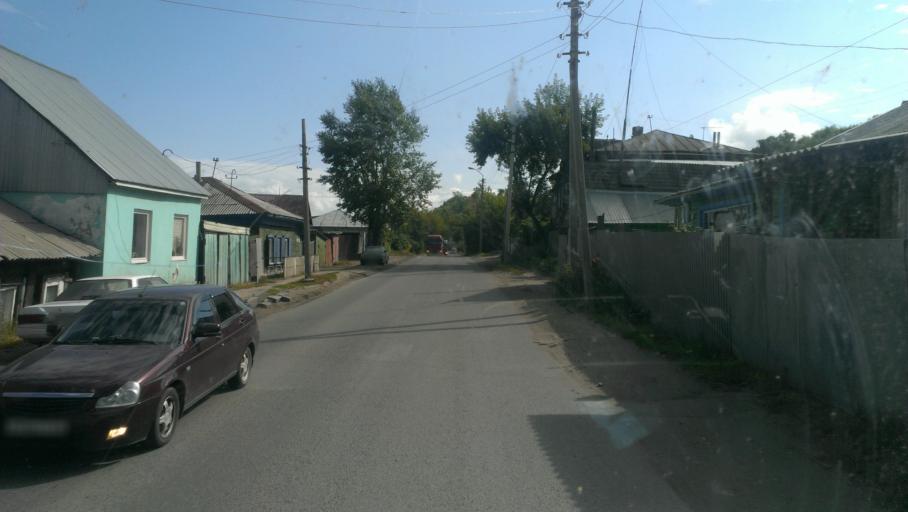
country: RU
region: Altai Krai
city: Zaton
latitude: 53.3197
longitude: 83.7749
